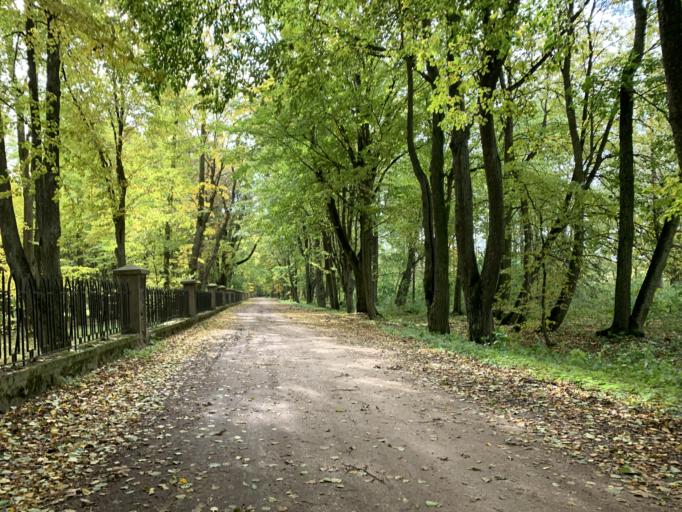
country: BY
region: Minsk
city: Nyasvizh
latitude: 53.2304
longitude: 26.6981
